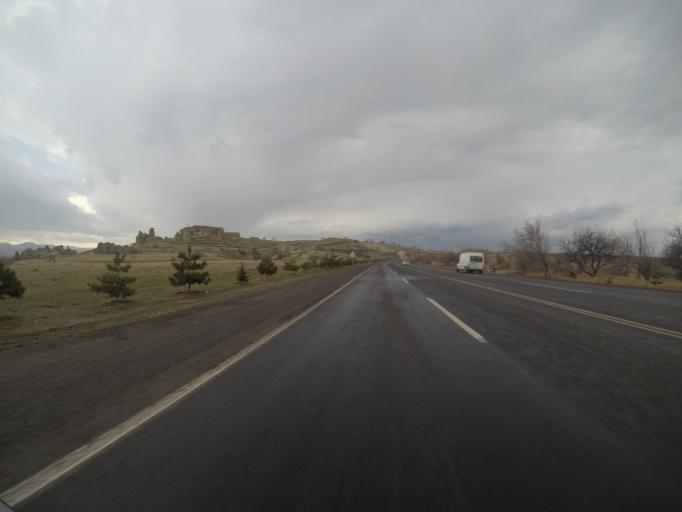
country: TR
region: Nevsehir
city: Urgub
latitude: 38.6356
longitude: 34.8860
